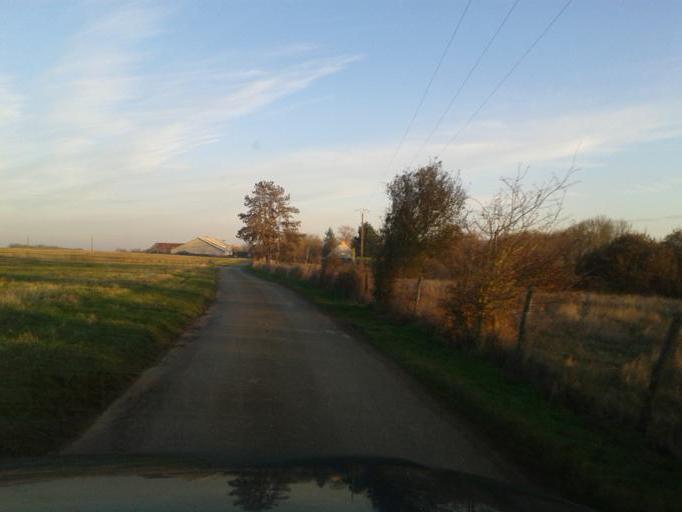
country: FR
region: Centre
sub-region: Departement du Loiret
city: Tavers
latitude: 47.7670
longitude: 1.5859
